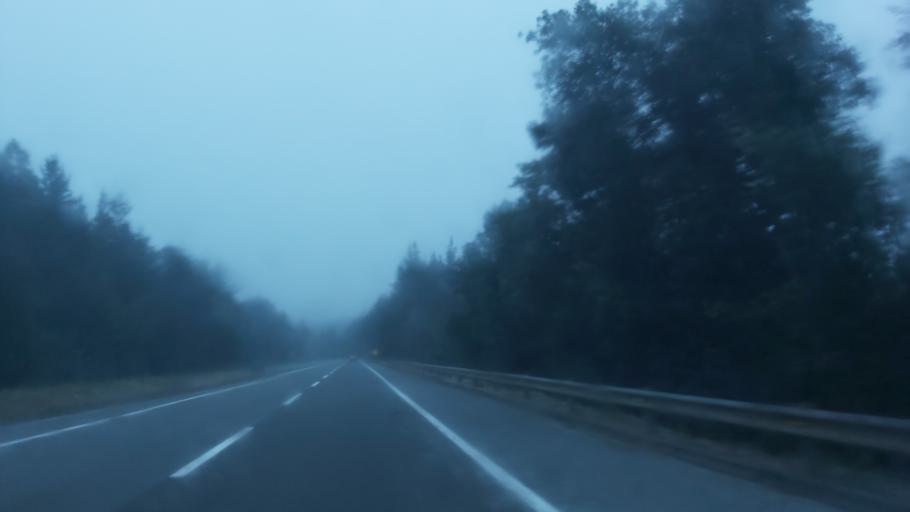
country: CL
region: Biobio
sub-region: Provincia de Concepcion
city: Penco
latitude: -36.7488
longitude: -72.9218
